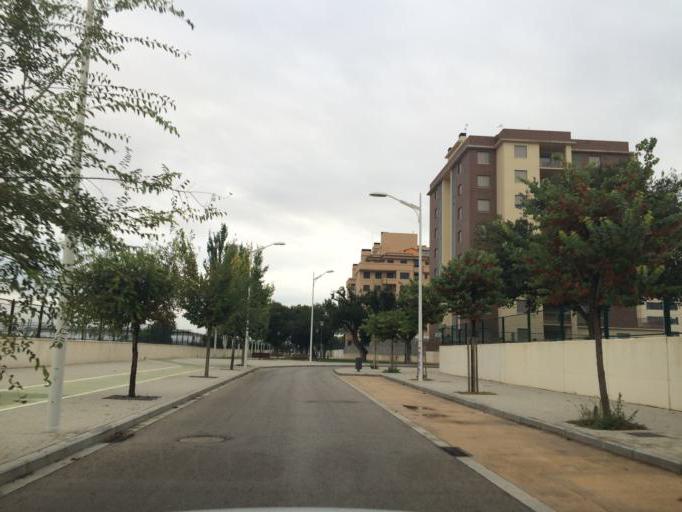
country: ES
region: Castille-La Mancha
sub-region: Provincia de Albacete
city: Albacete
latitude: 39.0079
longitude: -1.8572
